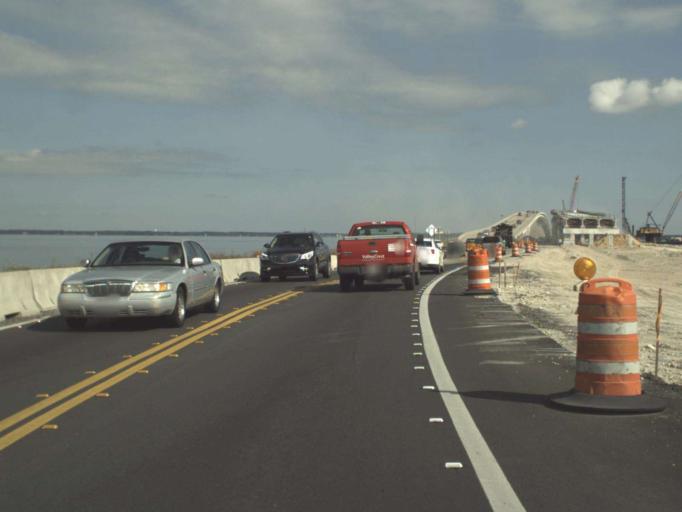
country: US
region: Florida
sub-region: Walton County
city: Seaside
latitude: 30.3929
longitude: -86.1720
